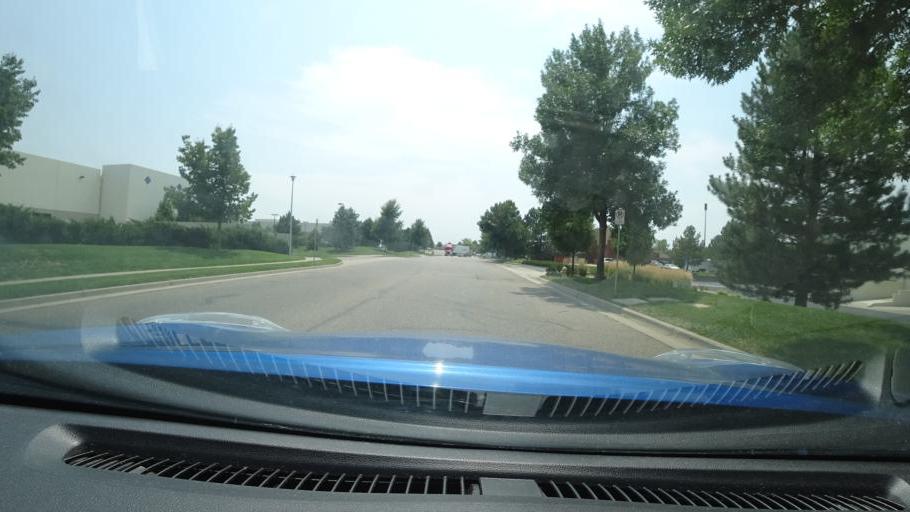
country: US
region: Colorado
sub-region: Adams County
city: Aurora
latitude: 39.7626
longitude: -104.7610
